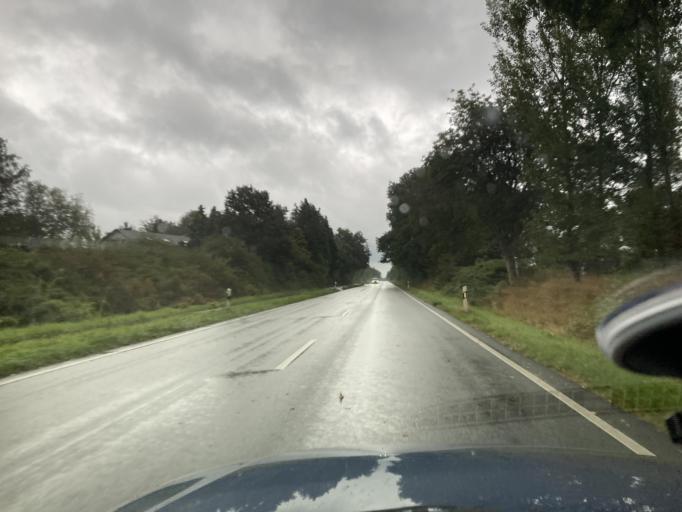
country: DE
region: Schleswig-Holstein
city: Suderdorf
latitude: 54.2187
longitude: 9.3583
